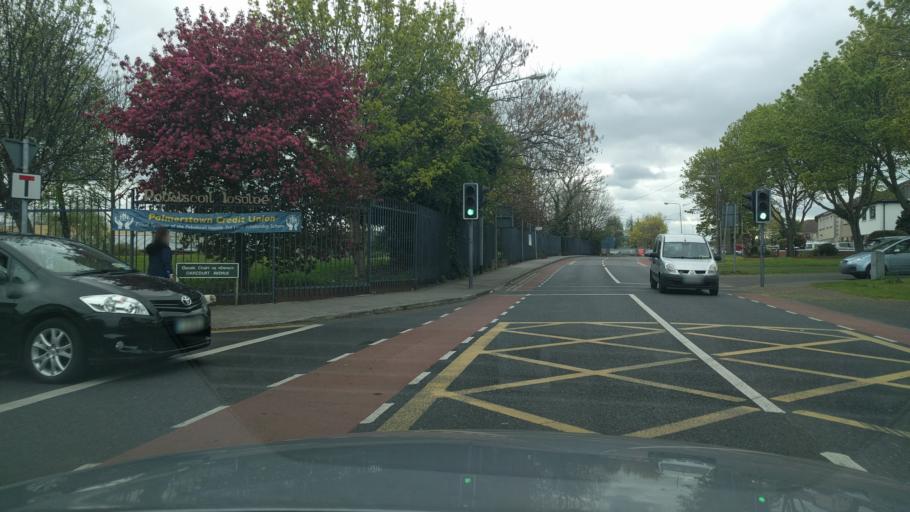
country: IE
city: Palmerstown
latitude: 53.3493
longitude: -6.3777
